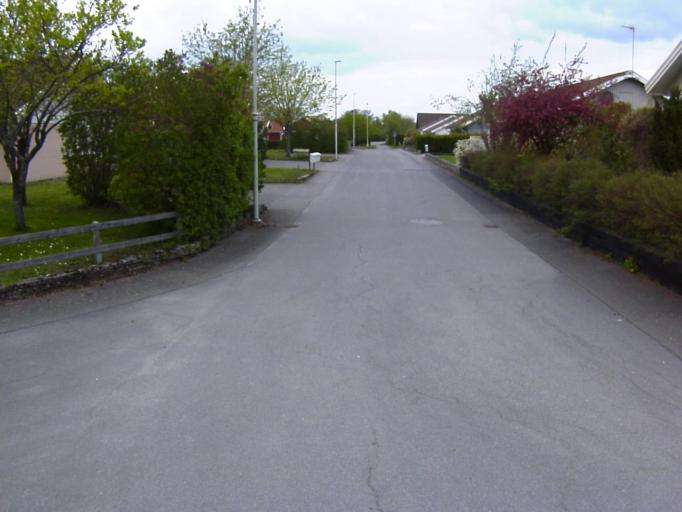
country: SE
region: Skane
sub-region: Kristianstads Kommun
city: Kristianstad
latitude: 56.0176
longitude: 14.1938
